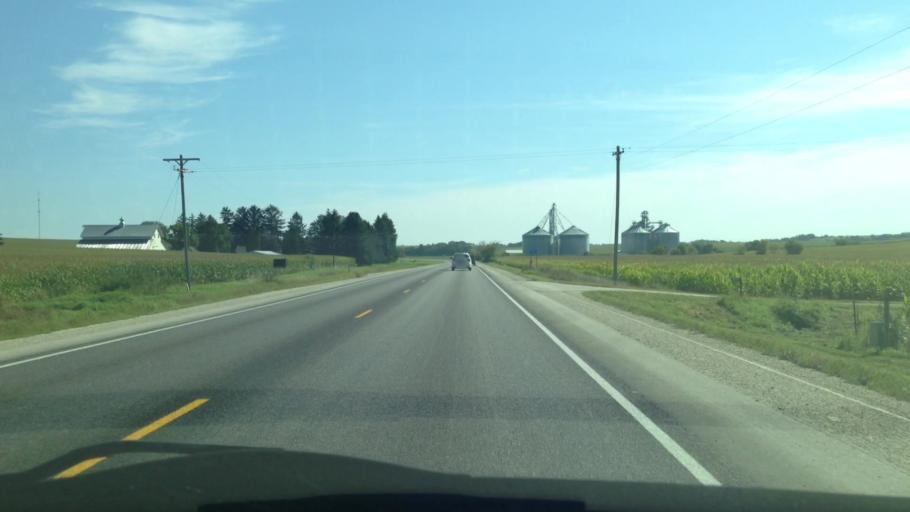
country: US
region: Minnesota
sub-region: Houston County
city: Spring Grove
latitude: 43.5150
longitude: -91.8021
